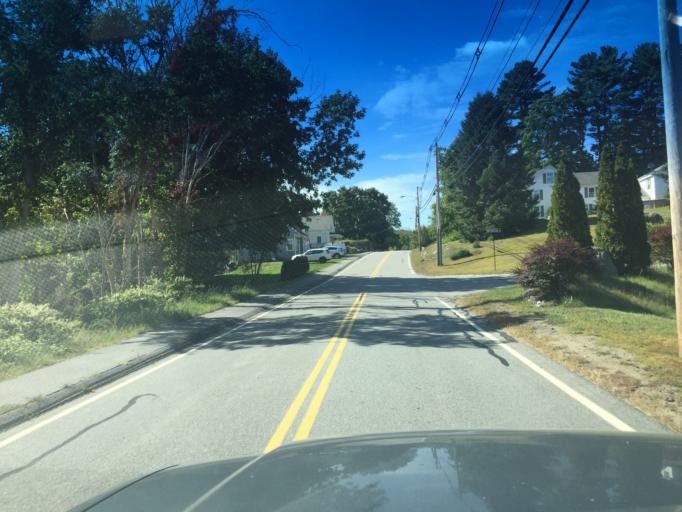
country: US
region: Massachusetts
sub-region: Worcester County
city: Northborough
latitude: 42.3269
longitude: -71.6340
